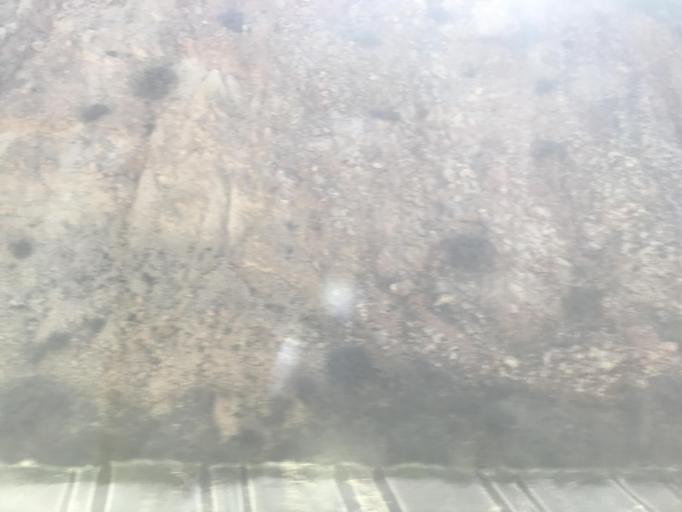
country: ES
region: Castille-La Mancha
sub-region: Provincia de Guadalajara
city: Anguita
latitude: 41.1082
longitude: -2.3677
